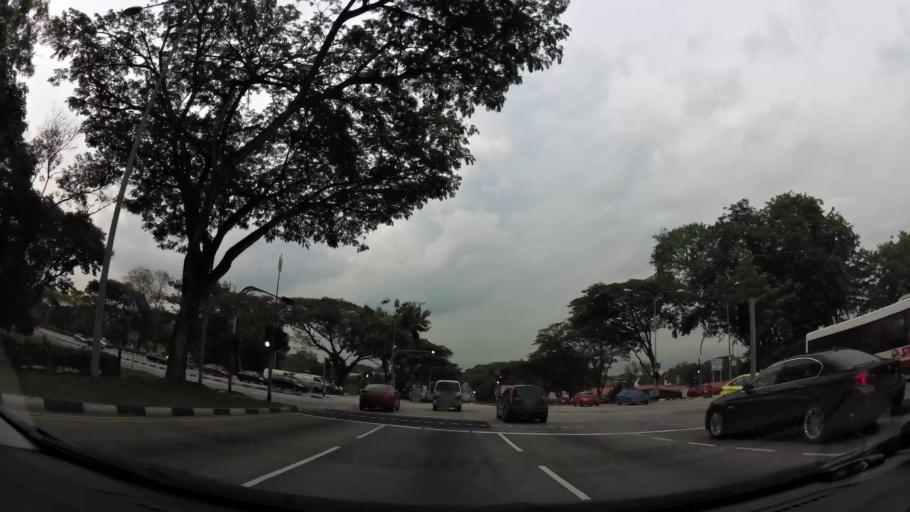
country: MY
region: Johor
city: Kampung Pasir Gudang Baru
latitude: 1.4132
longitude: 103.8229
